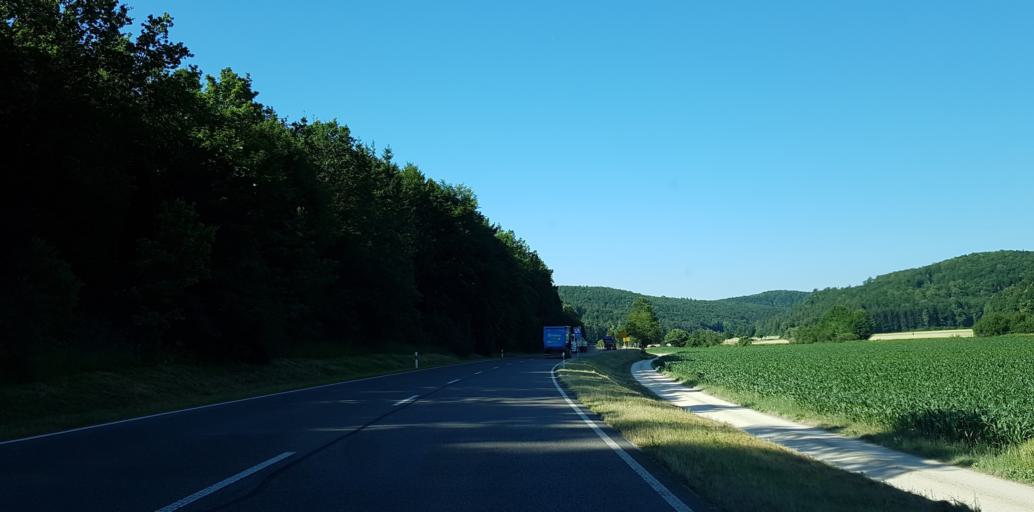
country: DE
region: Baden-Wuerttemberg
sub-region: Tuebingen Region
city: Allmendingen
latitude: 48.3526
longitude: 9.7170
